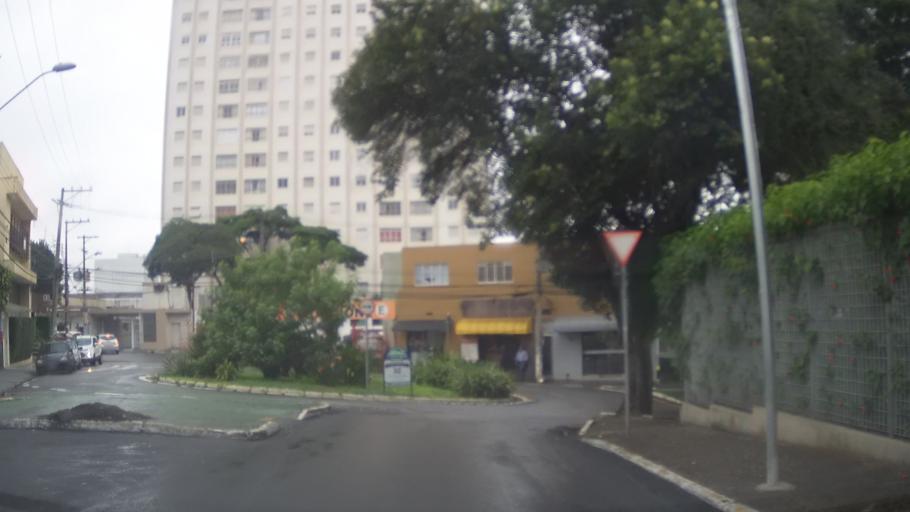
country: BR
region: Sao Paulo
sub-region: Guarulhos
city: Guarulhos
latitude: -23.4679
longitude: -46.5319
